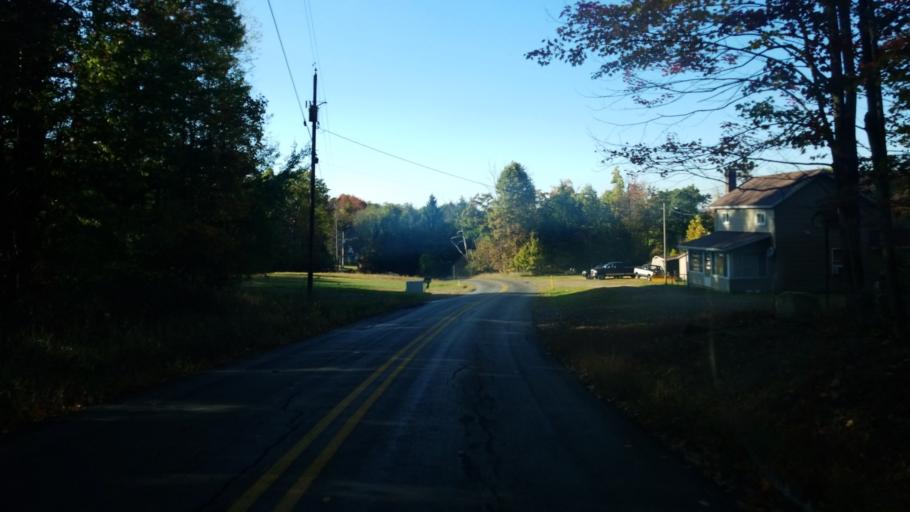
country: US
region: Pennsylvania
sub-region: Indiana County
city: Johnsonburg
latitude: 40.8969
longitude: -78.8926
